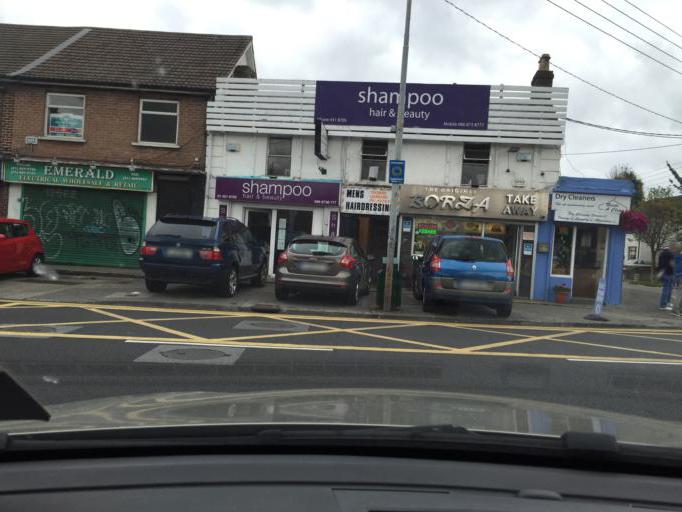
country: IE
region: Leinster
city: Templeogue
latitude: 53.3074
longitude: -6.3193
